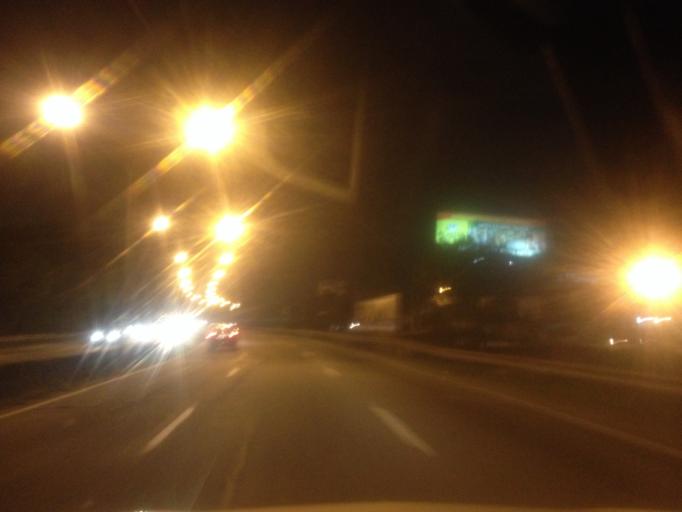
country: BR
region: Rio de Janeiro
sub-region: Duque De Caxias
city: Duque de Caxias
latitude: -22.8007
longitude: -43.3263
